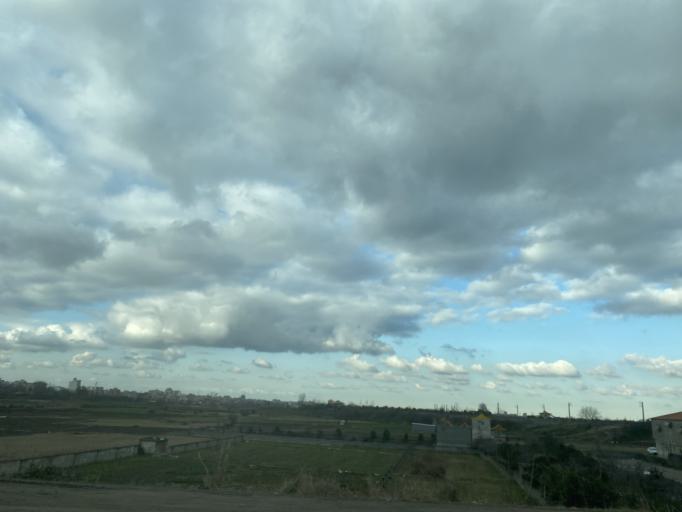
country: IR
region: Mazandaran
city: Amol
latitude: 36.4333
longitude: 52.3535
